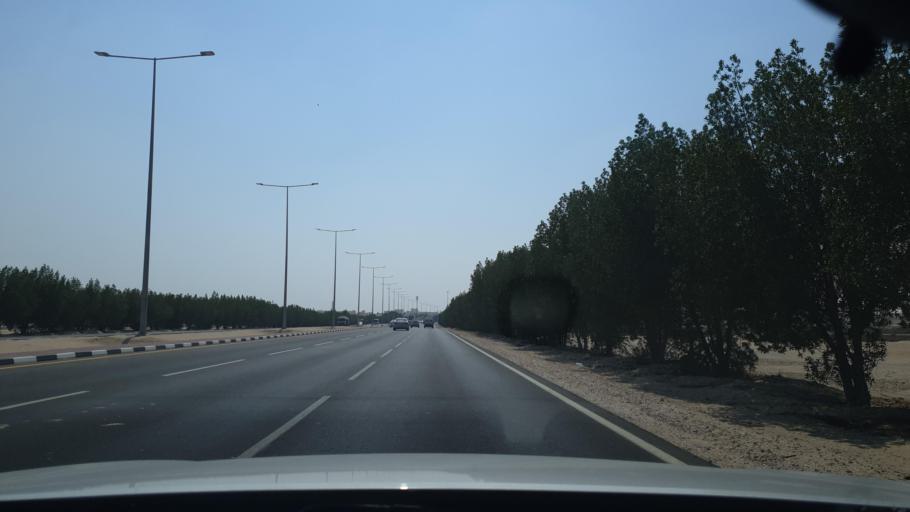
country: QA
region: Al Khawr
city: Al Khawr
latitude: 25.6970
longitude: 51.5020
